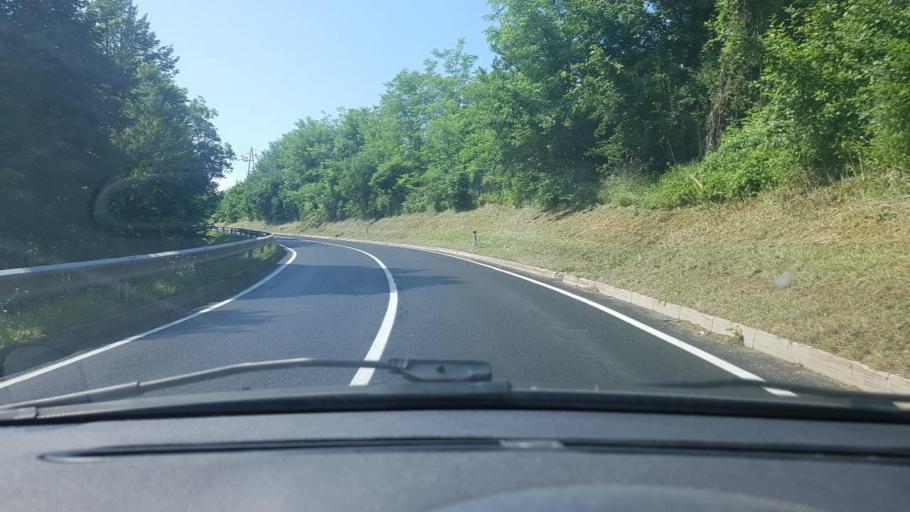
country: SI
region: Sentilj
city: Sentilj v Slov. Goricah
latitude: 46.6852
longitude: 15.6635
